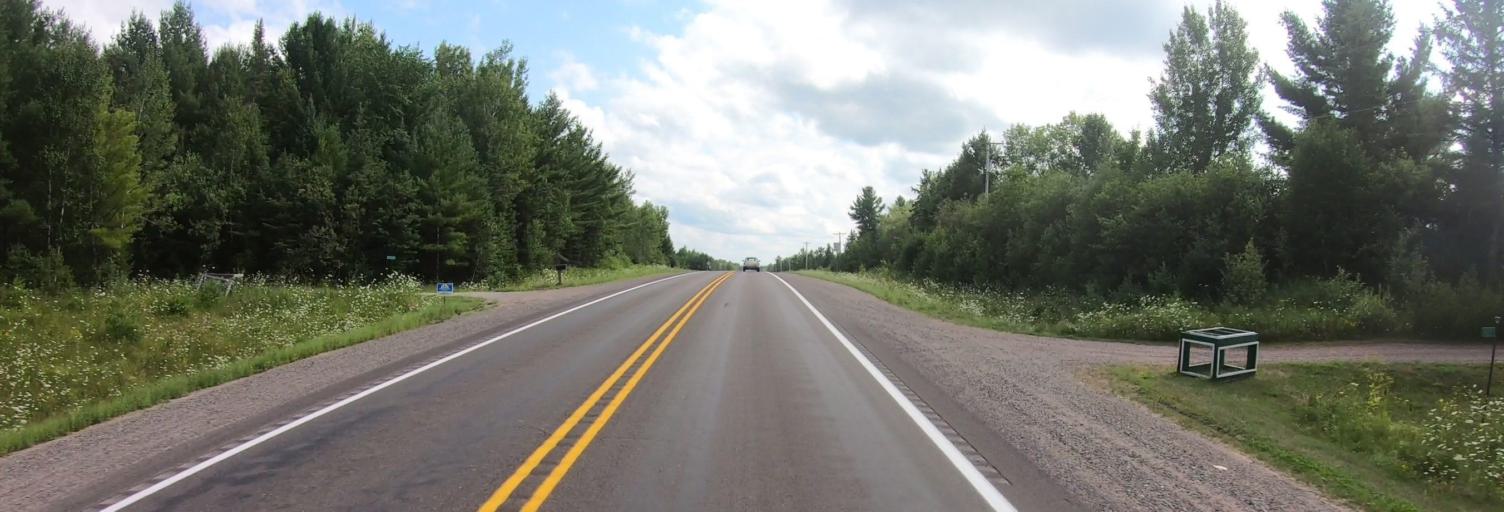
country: US
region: Michigan
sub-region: Ontonagon County
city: Ontonagon
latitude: 46.5544
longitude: -89.1786
